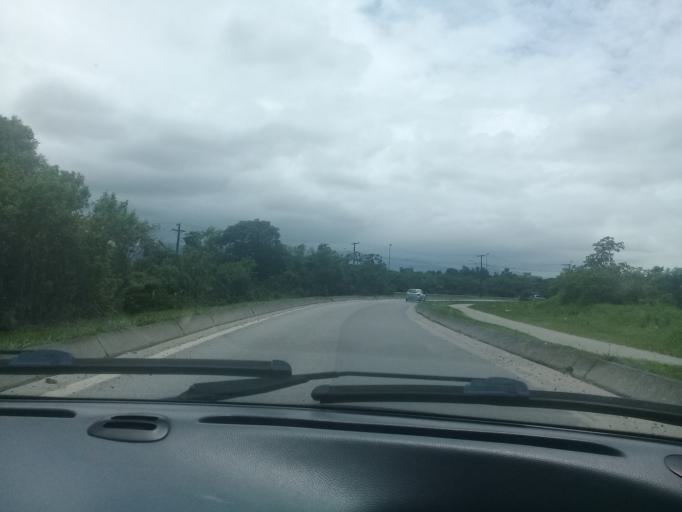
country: BR
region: Sao Paulo
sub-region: Guaruja
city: Guaruja
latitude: -23.9695
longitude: -46.2680
